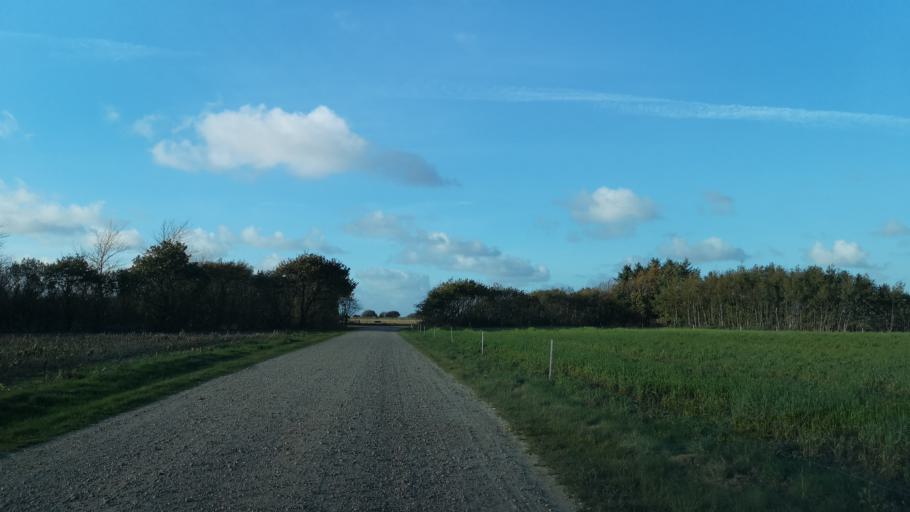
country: DK
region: Central Jutland
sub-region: Ringkobing-Skjern Kommune
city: Skjern
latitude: 55.8655
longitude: 8.3342
